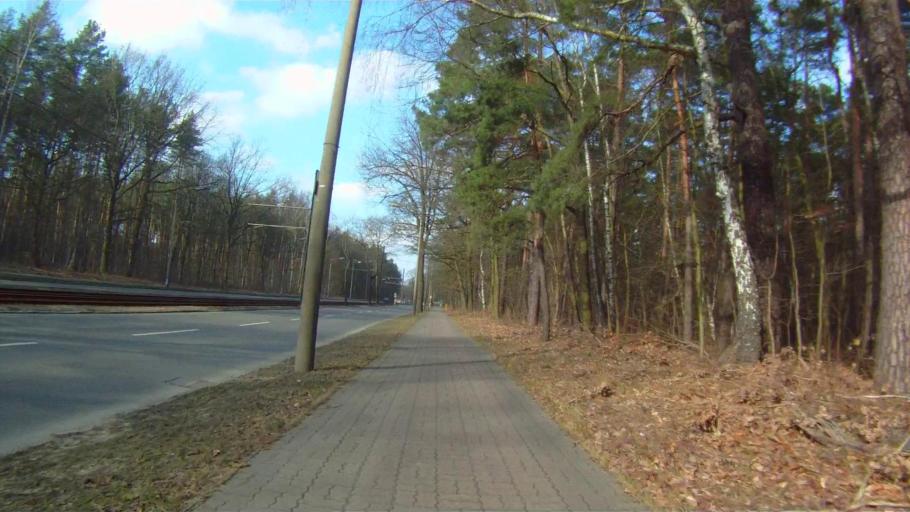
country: DE
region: Berlin
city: Schmockwitz
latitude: 52.3837
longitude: 13.6376
